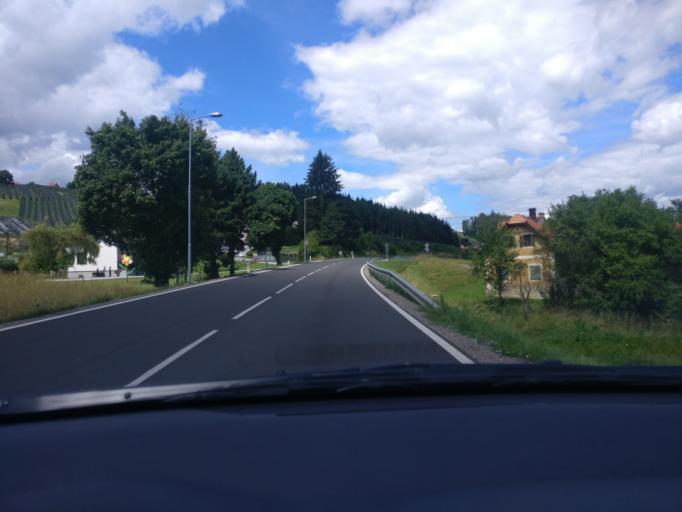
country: AT
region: Styria
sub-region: Politischer Bezirk Weiz
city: Gleisdorf
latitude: 47.1203
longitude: 15.7152
